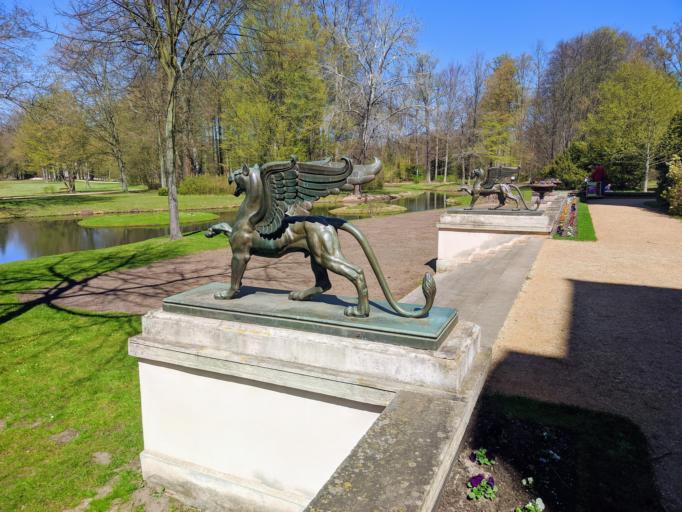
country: DE
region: Brandenburg
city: Cottbus
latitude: 51.7420
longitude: 14.3687
